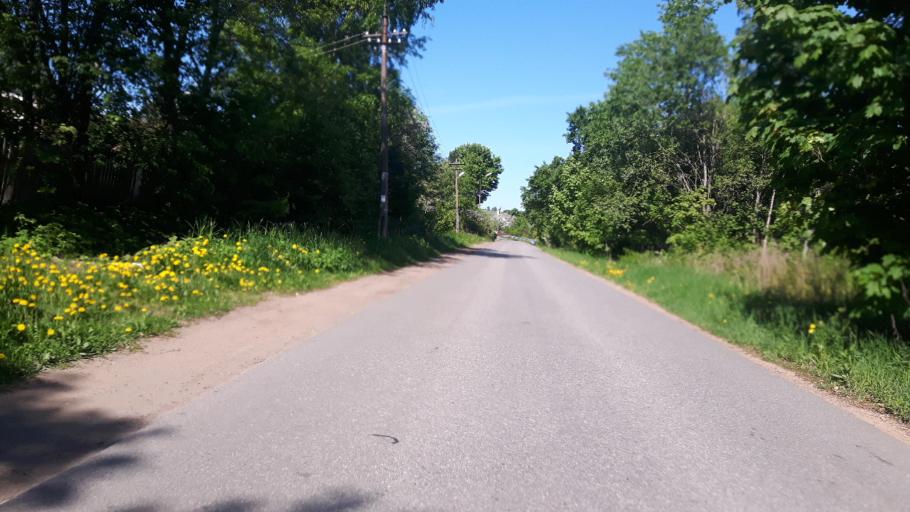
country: RU
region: Leningrad
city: Lebyazh'ye
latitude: 59.9710
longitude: 29.3837
